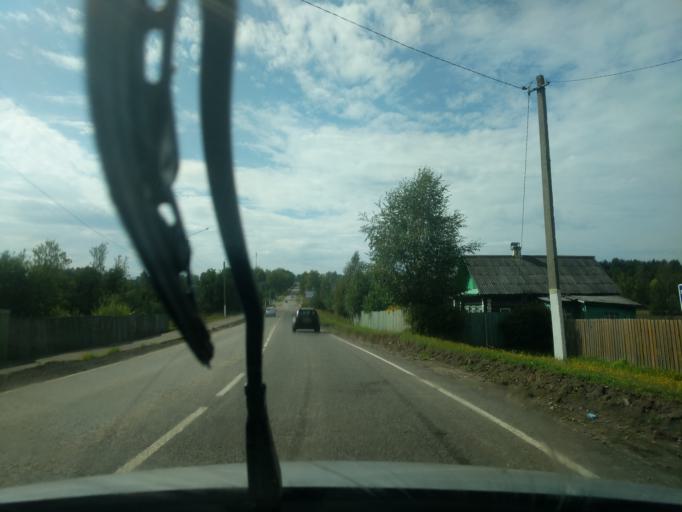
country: RU
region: Kostroma
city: Sudislavl'
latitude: 57.8817
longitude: 41.7028
